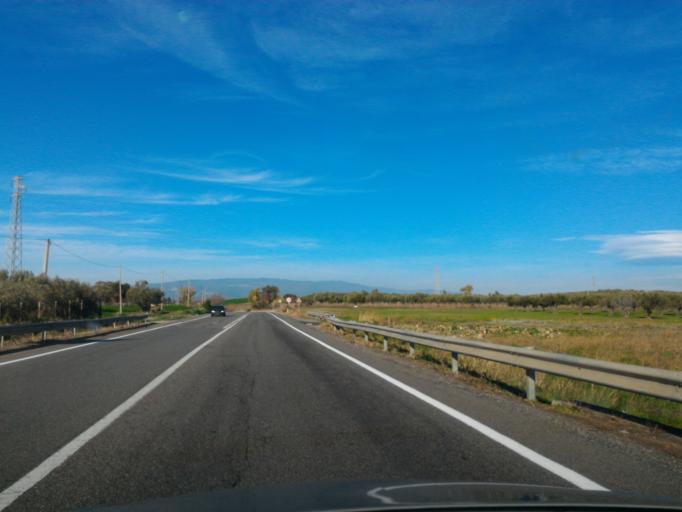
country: IT
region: Calabria
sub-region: Provincia di Crotone
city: Le Castella
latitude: 38.9366
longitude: 17.0035
